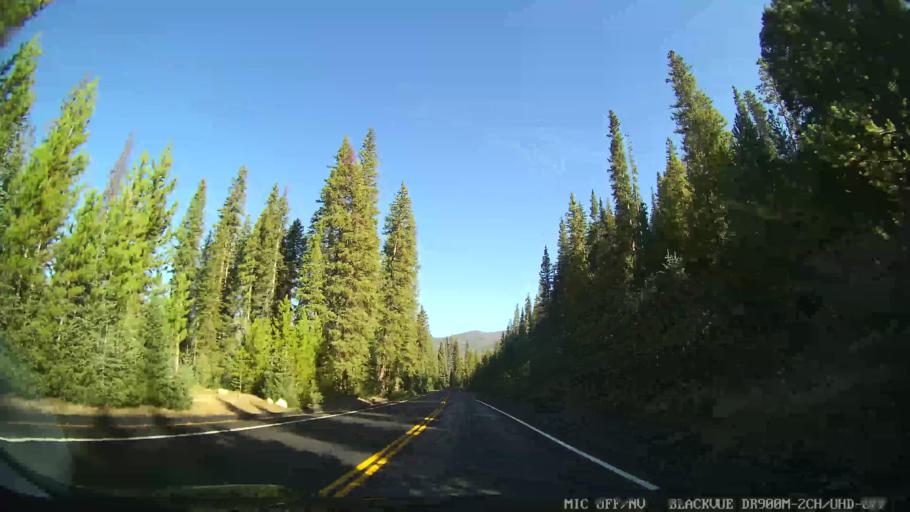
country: US
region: Colorado
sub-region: Grand County
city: Granby
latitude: 40.3028
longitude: -105.8427
